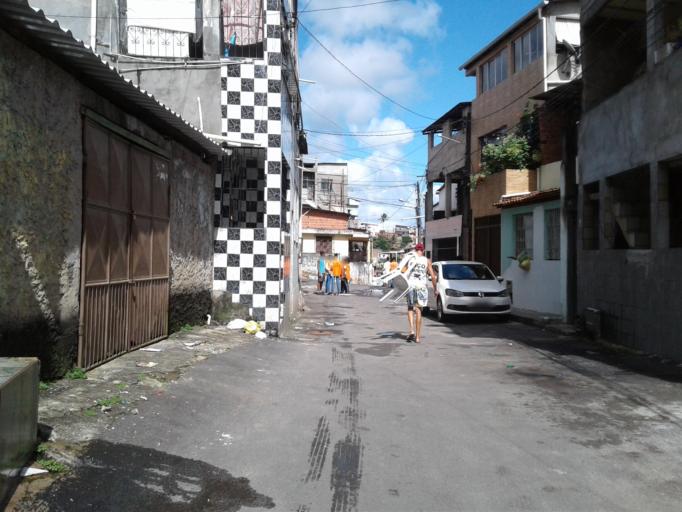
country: BR
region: Bahia
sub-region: Salvador
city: Salvador
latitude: -12.9116
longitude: -38.4716
